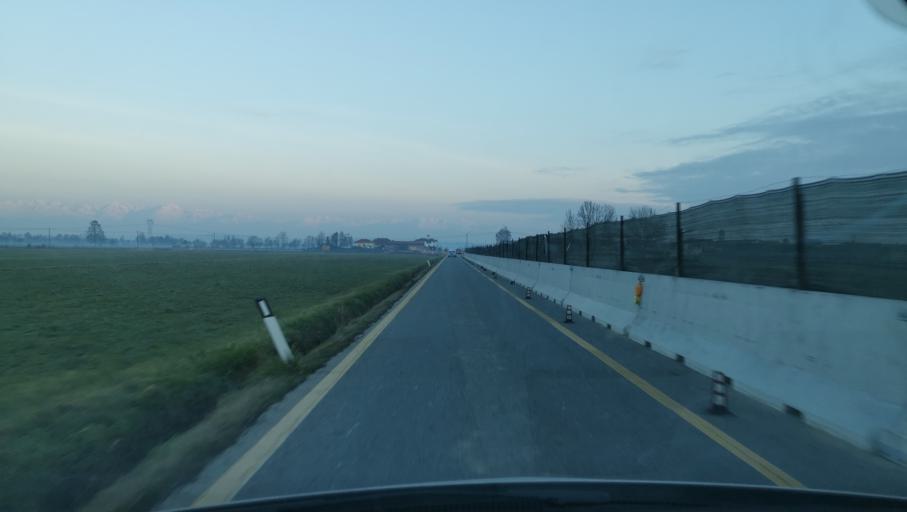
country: IT
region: Piedmont
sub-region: Provincia di Torino
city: Montanaro
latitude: 45.2508
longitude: 7.8917
